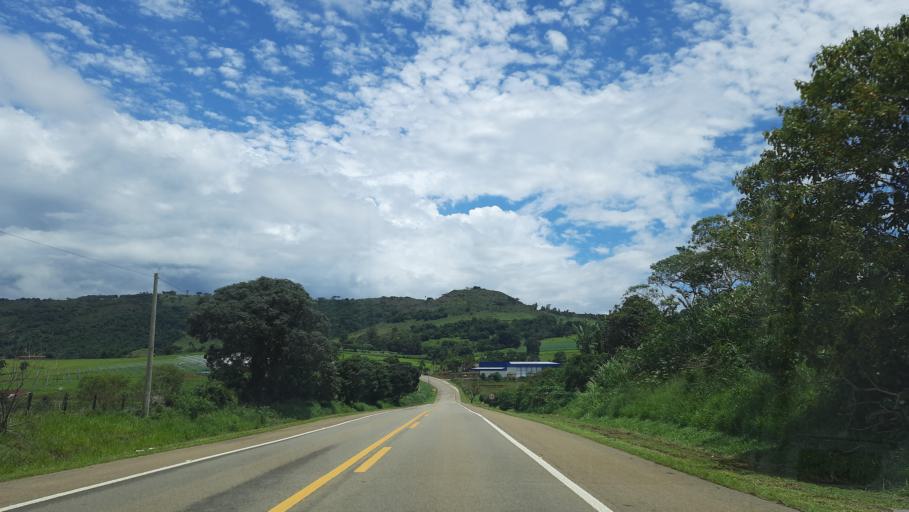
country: BR
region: Sao Paulo
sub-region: Vargem Grande Do Sul
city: Vargem Grande do Sul
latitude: -21.8178
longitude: -46.7844
